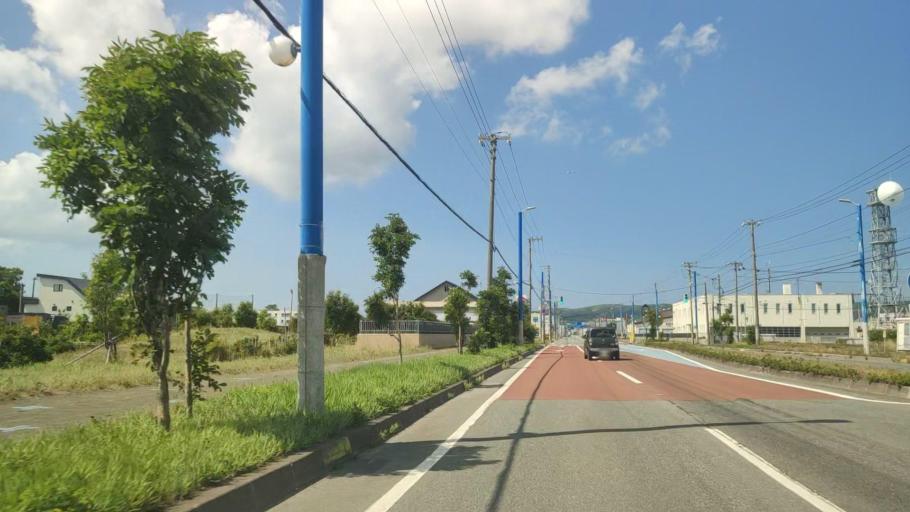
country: JP
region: Hokkaido
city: Wakkanai
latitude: 45.3950
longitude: 141.7122
